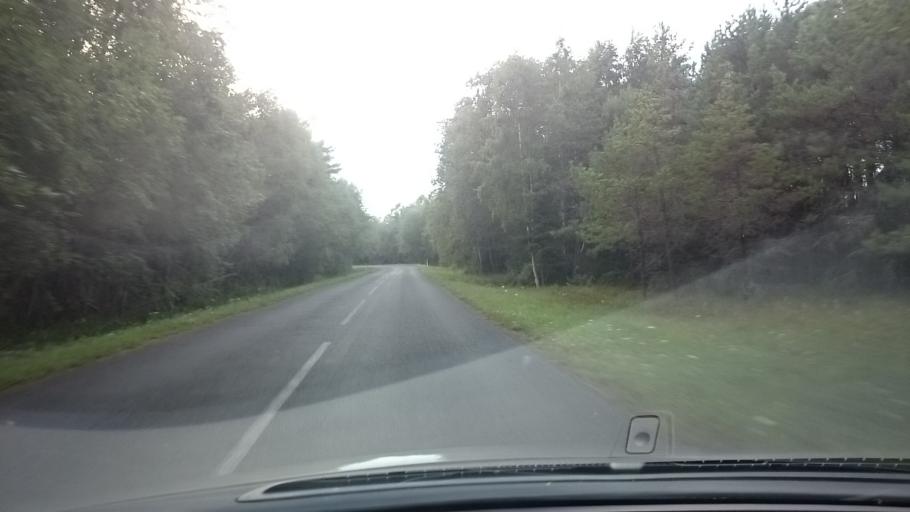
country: EE
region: Saare
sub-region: Kuressaare linn
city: Kuressaare
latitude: 58.4146
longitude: 22.0914
